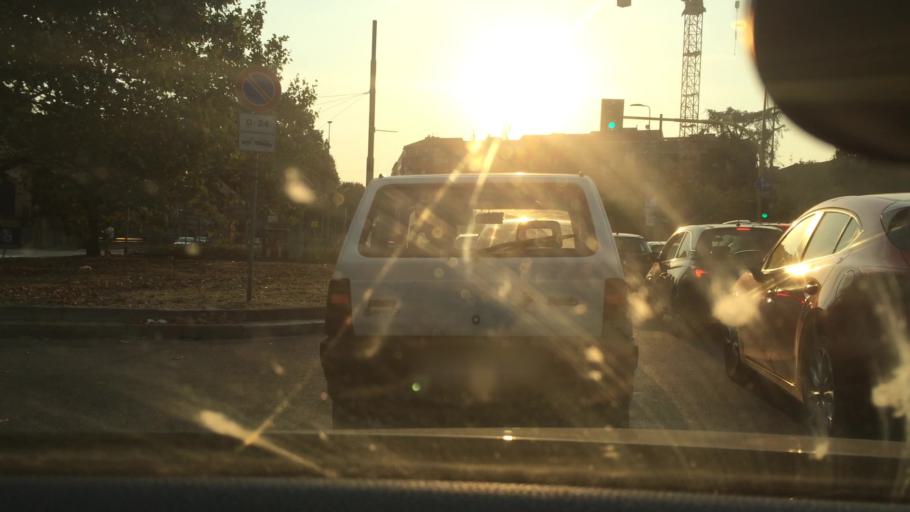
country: IT
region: Lombardy
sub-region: Citta metropolitana di Milano
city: Milano
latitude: 45.4977
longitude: 9.1873
